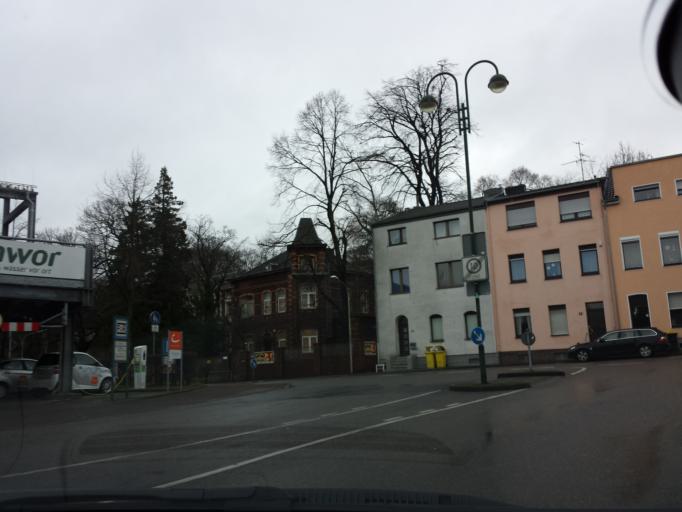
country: DE
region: North Rhine-Westphalia
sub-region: Regierungsbezirk Koln
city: Herzogenrath
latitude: 50.8713
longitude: 6.0952
